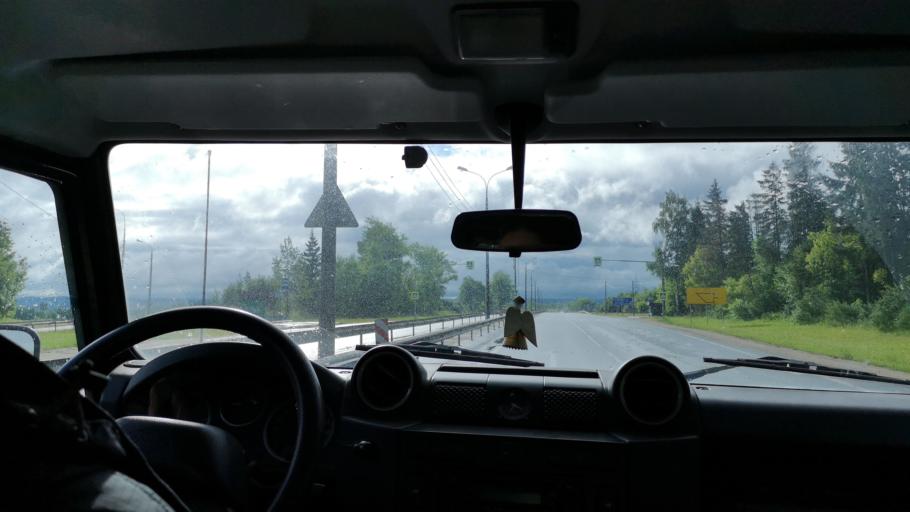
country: RU
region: Moskovskaya
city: Dmitrov
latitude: 56.3659
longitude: 37.4693
